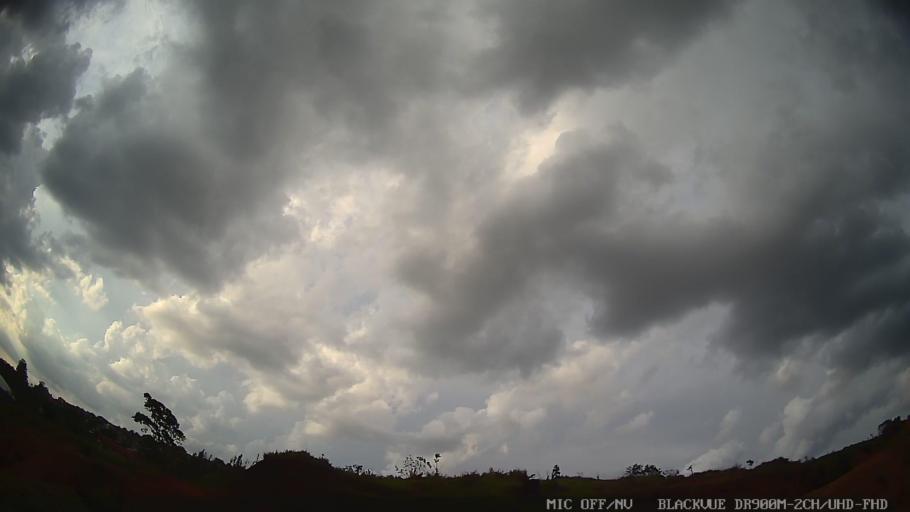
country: BR
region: Sao Paulo
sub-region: Braganca Paulista
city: Braganca Paulista
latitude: -22.9299
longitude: -46.5297
